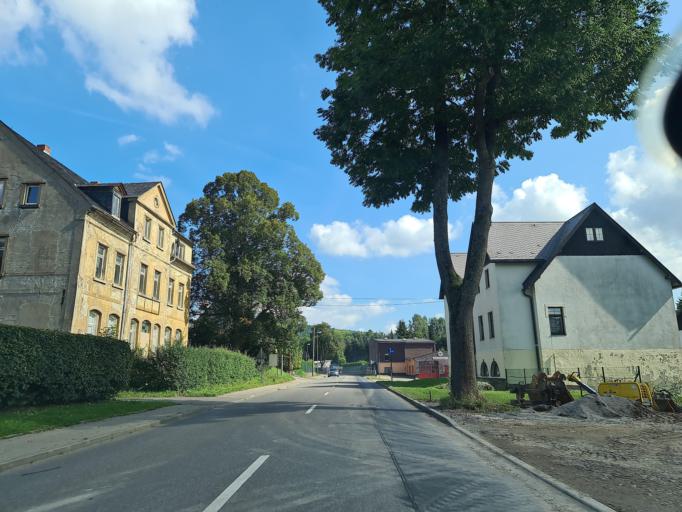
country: DE
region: Saxony
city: Heidersdorf
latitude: 50.6476
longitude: 13.3824
